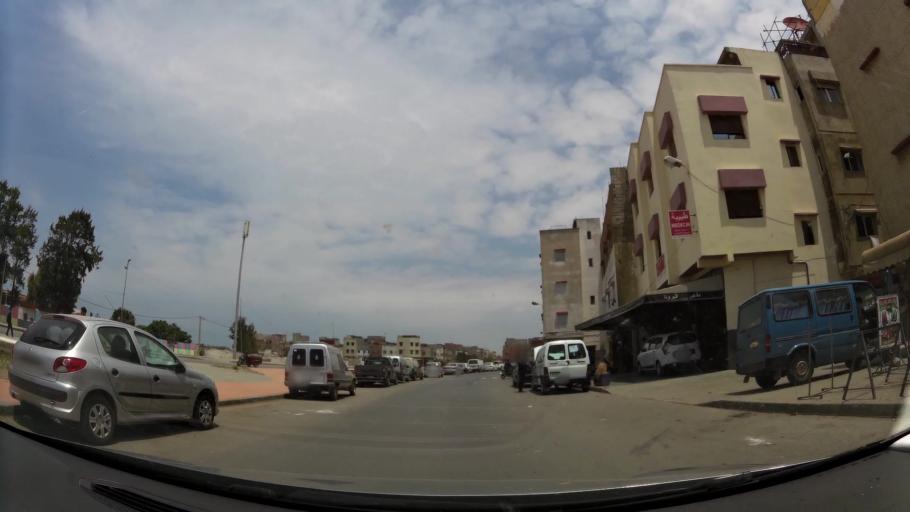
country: MA
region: Rabat-Sale-Zemmour-Zaer
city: Sale
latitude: 34.0688
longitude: -6.7773
